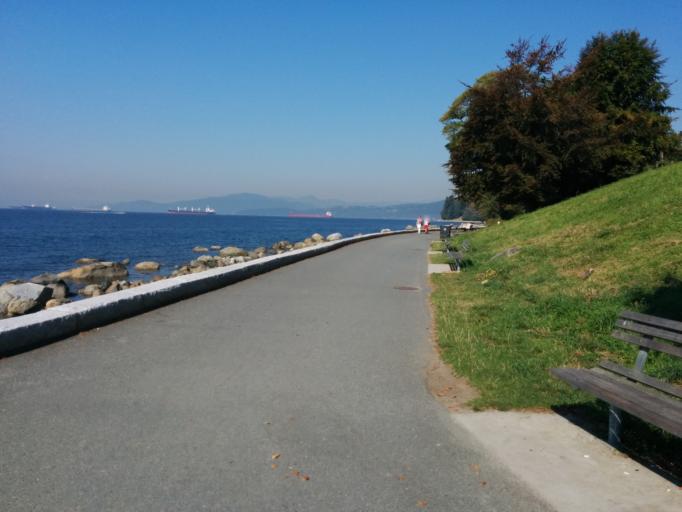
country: CA
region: British Columbia
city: West End
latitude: 49.2904
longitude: -123.1470
